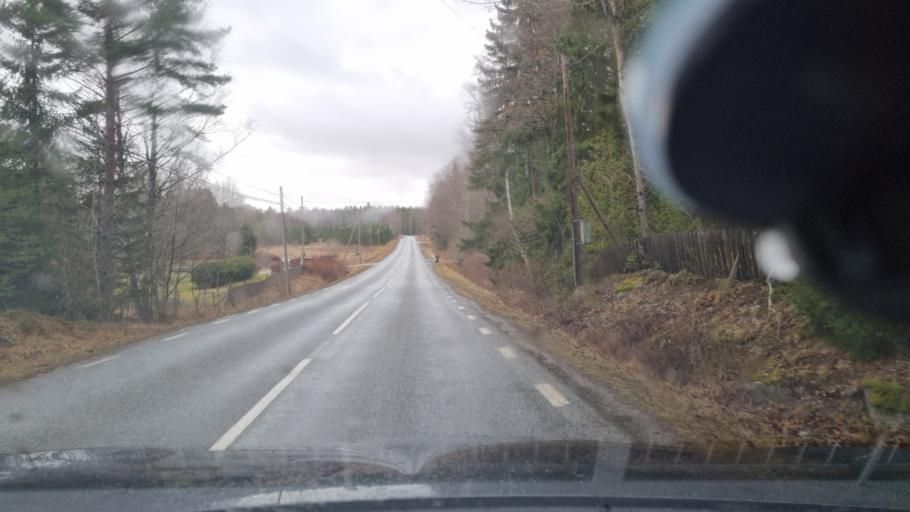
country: SE
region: Stockholm
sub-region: Sigtuna Kommun
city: Sigtuna
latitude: 59.5694
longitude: 17.6859
